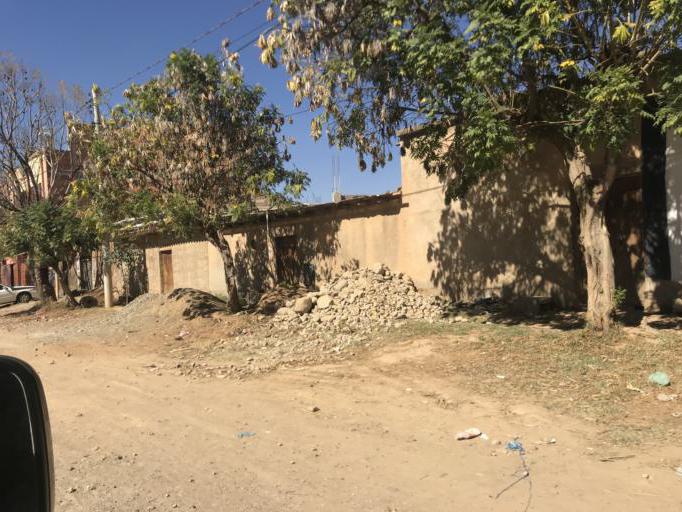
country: BO
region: Cochabamba
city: Cliza
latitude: -17.5830
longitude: -65.9150
